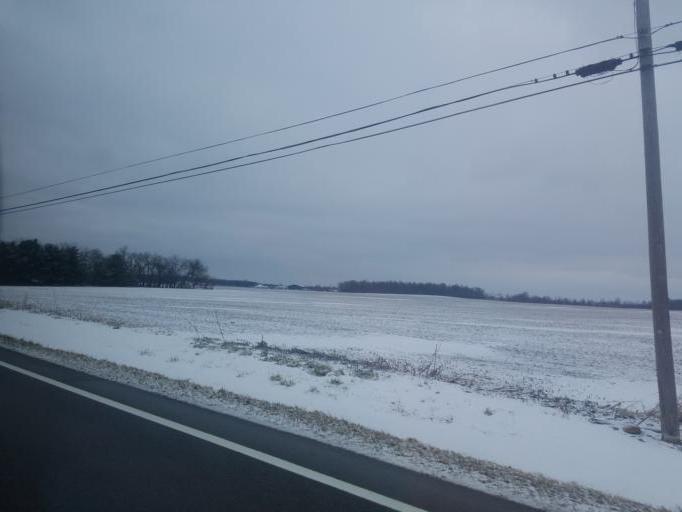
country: US
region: Ohio
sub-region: Licking County
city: Johnstown
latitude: 40.1841
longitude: -82.7489
